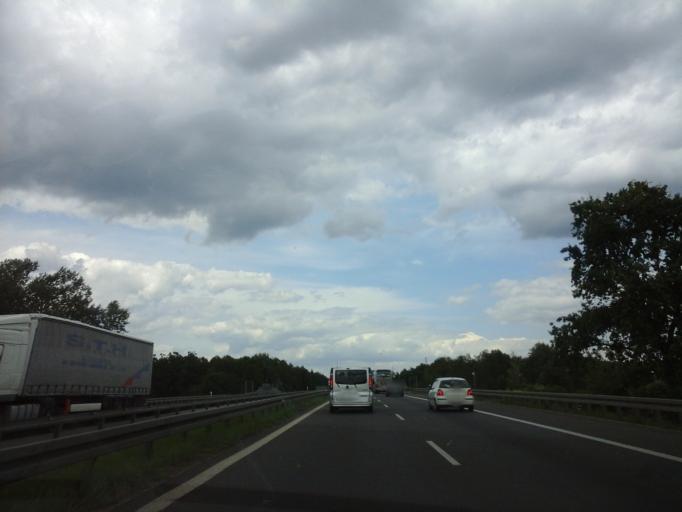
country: PL
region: West Pomeranian Voivodeship
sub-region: Powiat gryfinski
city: Stare Czarnowo
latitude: 53.3873
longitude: 14.7144
